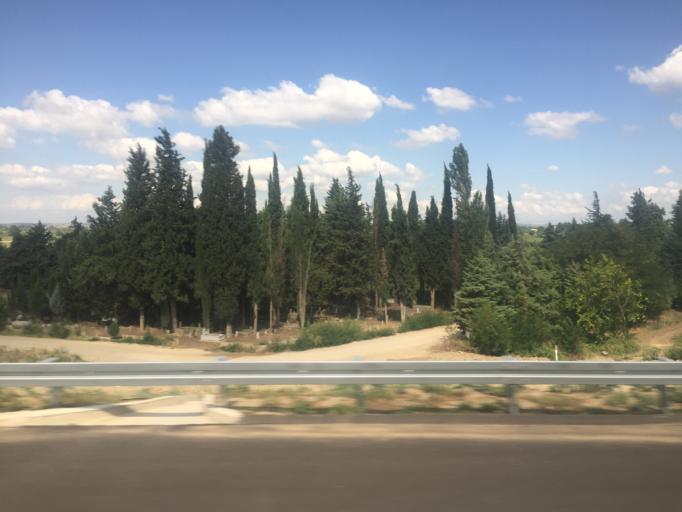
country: TR
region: Balikesir
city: Gobel
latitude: 40.0701
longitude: 28.2502
